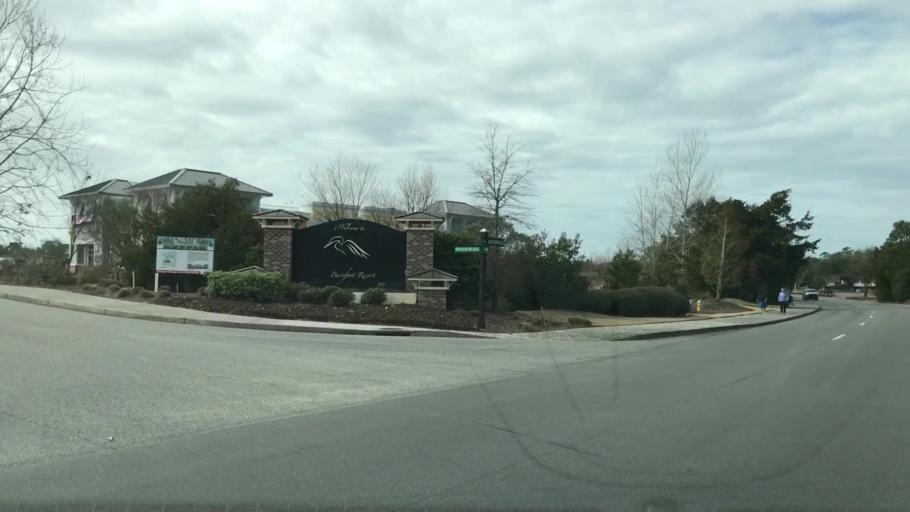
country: US
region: South Carolina
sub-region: Horry County
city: North Myrtle Beach
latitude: 33.8067
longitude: -78.7467
